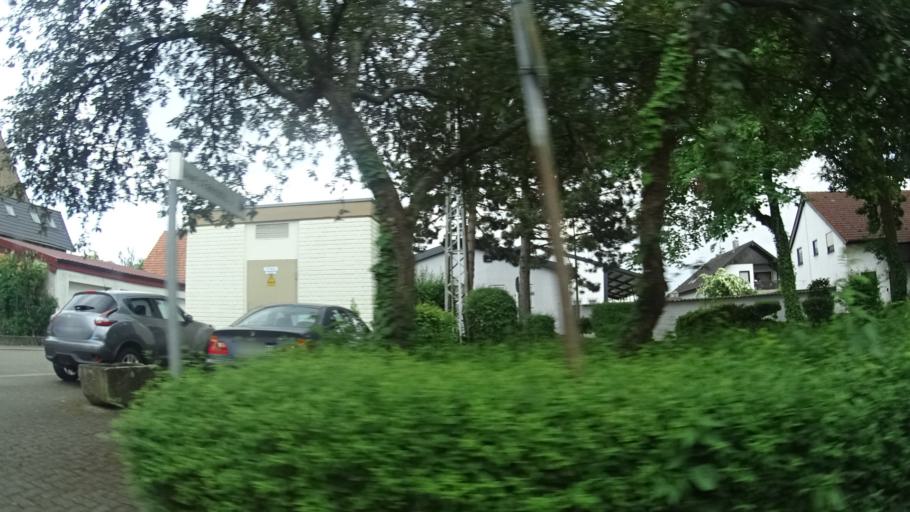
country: DE
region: Rheinland-Pfalz
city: Lustadt
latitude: 49.2447
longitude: 8.2826
